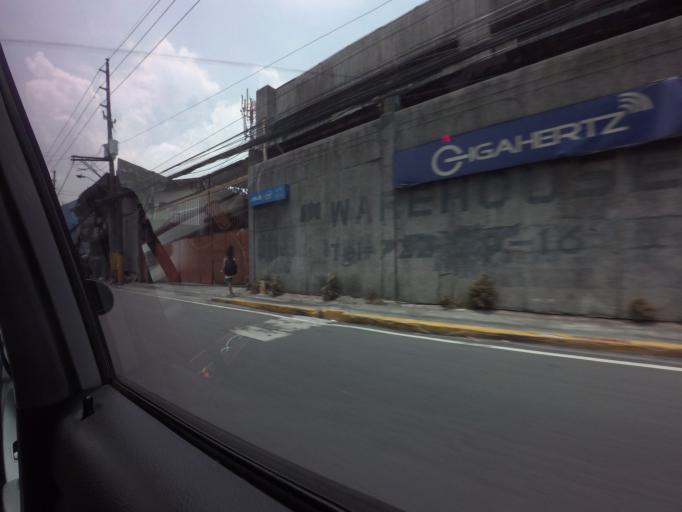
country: PH
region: Metro Manila
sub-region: City of Manila
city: Quiapo
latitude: 14.5952
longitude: 120.9888
